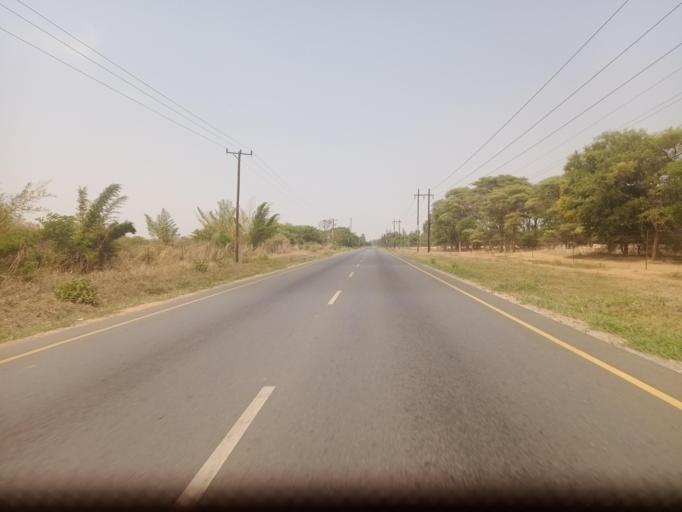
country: ZM
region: Lusaka
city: Lusaka
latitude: -15.2829
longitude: 28.3876
